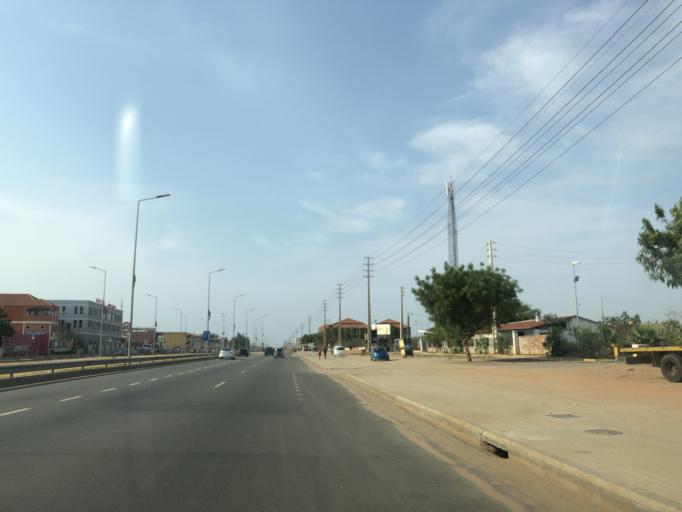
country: AO
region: Luanda
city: Luanda
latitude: -8.9243
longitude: 13.2629
